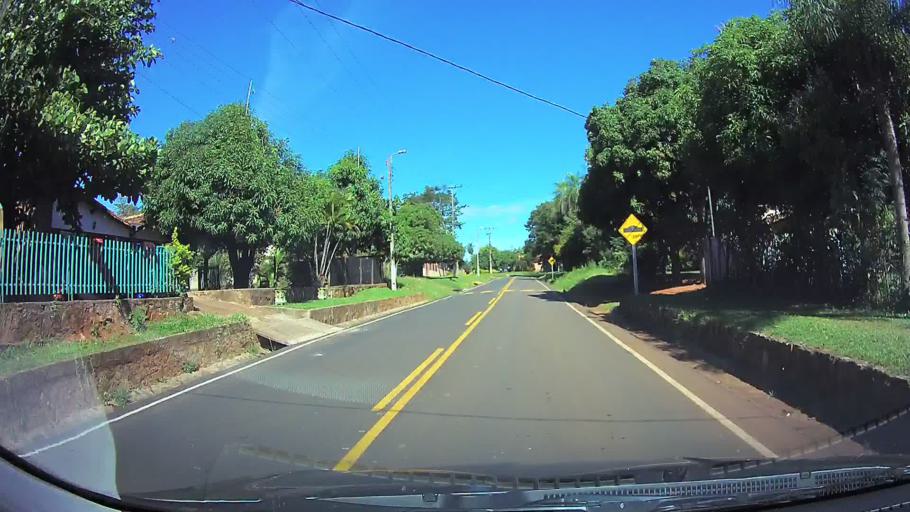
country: PY
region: Central
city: Aregua
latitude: -25.2486
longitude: -57.4380
